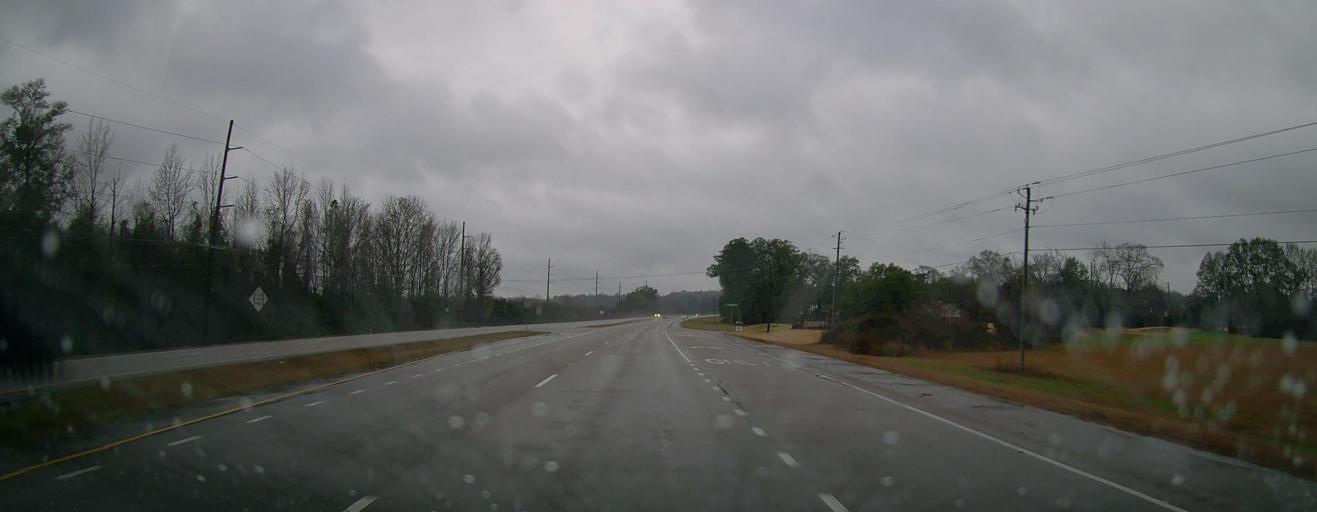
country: US
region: Alabama
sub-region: Autauga County
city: Prattville
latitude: 32.4419
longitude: -86.4800
